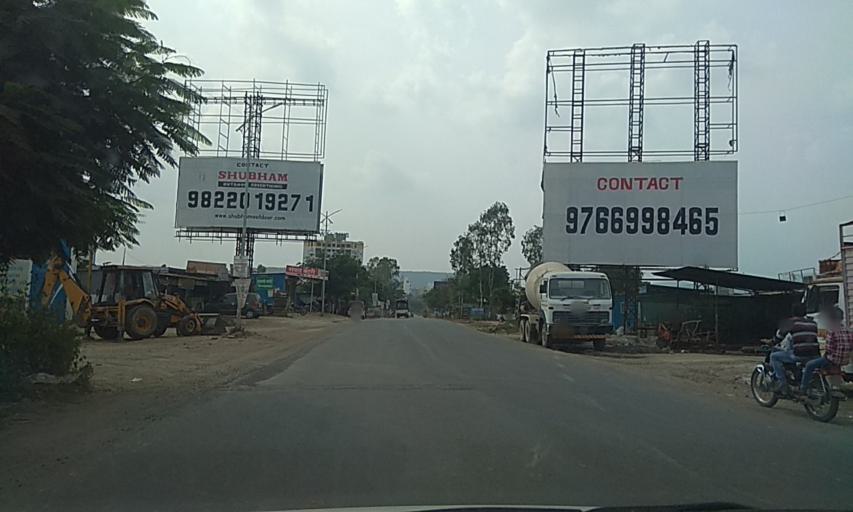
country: IN
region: Maharashtra
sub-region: Pune Division
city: Pimpri
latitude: 18.5785
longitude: 73.7162
